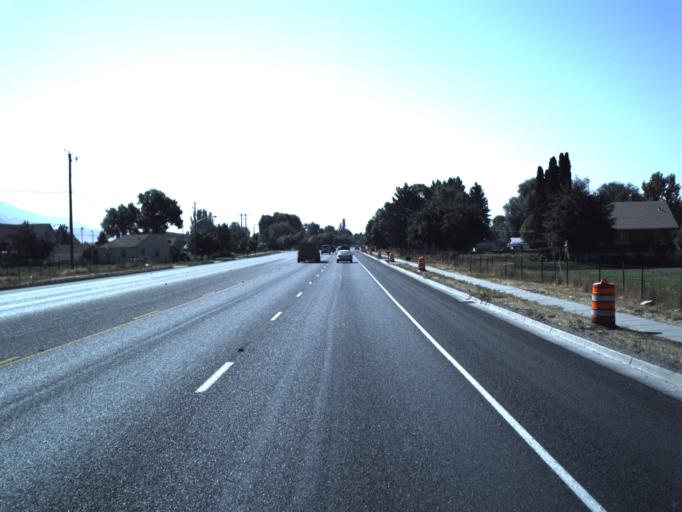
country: US
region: Utah
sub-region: Cache County
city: Nibley
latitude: 41.6795
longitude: -111.8336
